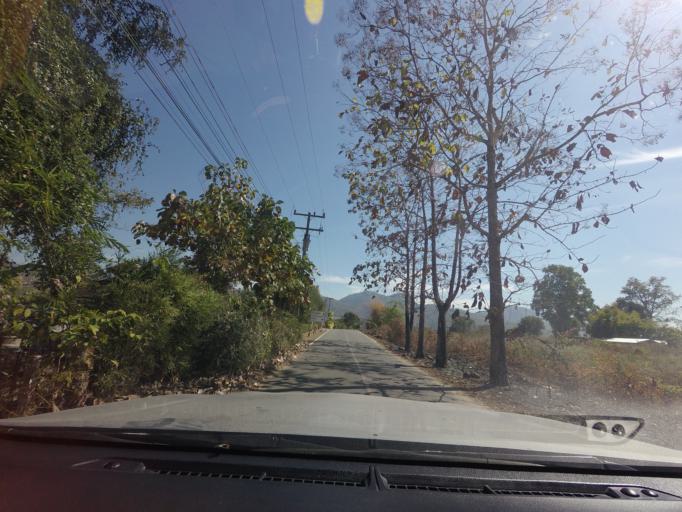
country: TH
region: Mae Hong Son
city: Wiang Nuea
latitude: 19.3860
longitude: 98.4365
